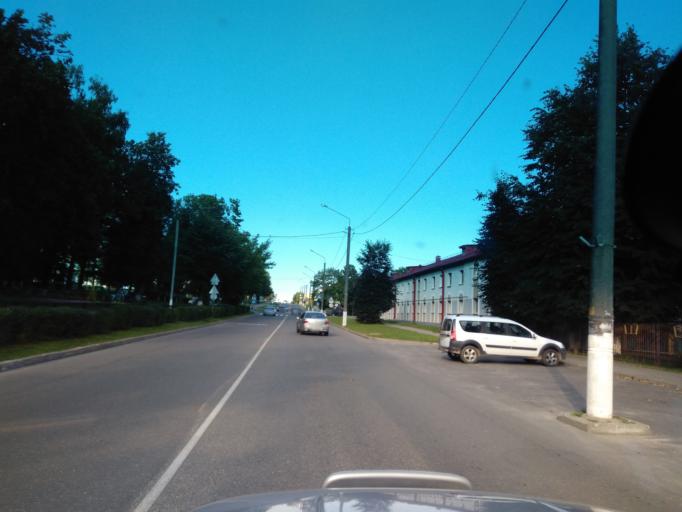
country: BY
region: Minsk
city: Dzyarzhynsk
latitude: 53.6831
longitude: 27.1277
